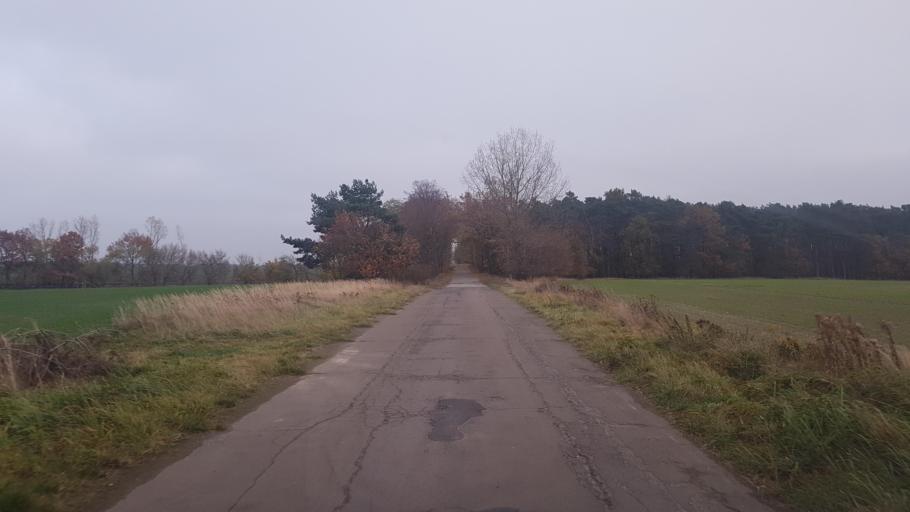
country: DE
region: Brandenburg
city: Gross Kreutz
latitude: 52.3715
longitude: 12.8129
